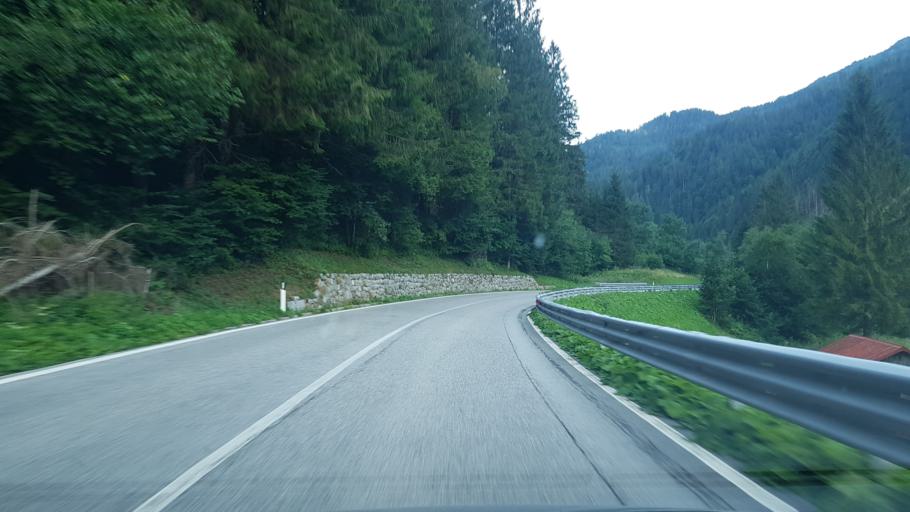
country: IT
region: Friuli Venezia Giulia
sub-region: Provincia di Udine
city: Forni Avoltri
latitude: 46.5793
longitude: 12.7899
